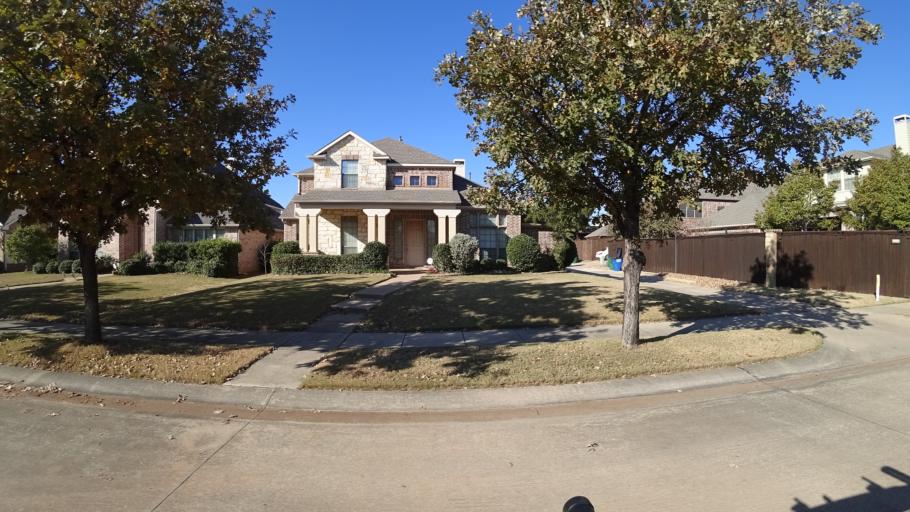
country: US
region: Texas
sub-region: Denton County
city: The Colony
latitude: 33.0365
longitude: -96.9169
